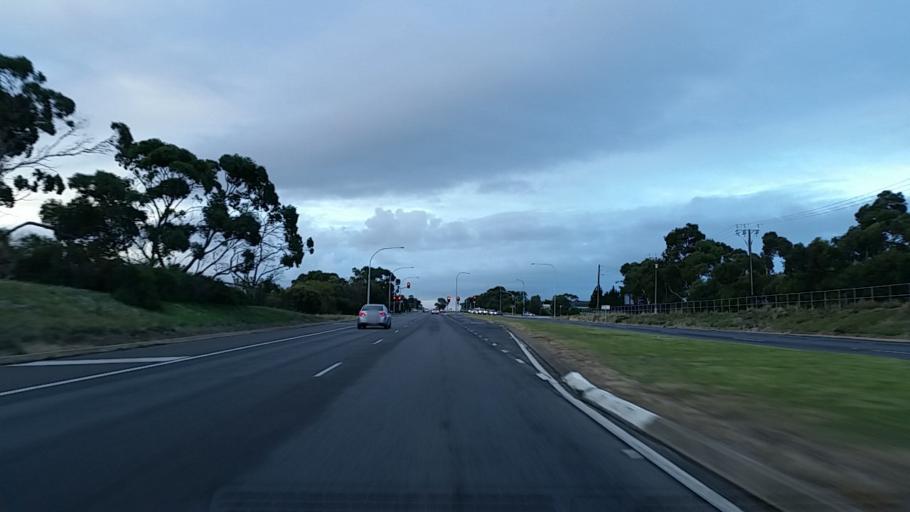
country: AU
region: South Australia
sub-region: Marion
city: Happy Valley
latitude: -35.0734
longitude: 138.5240
